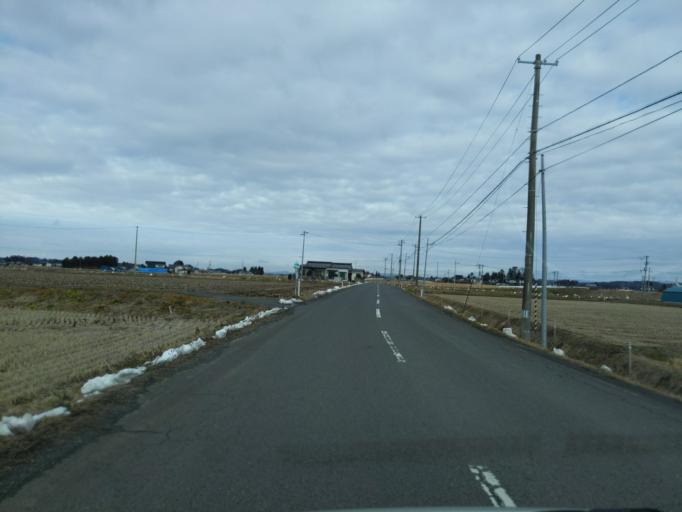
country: JP
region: Iwate
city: Mizusawa
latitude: 39.0794
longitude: 141.1652
